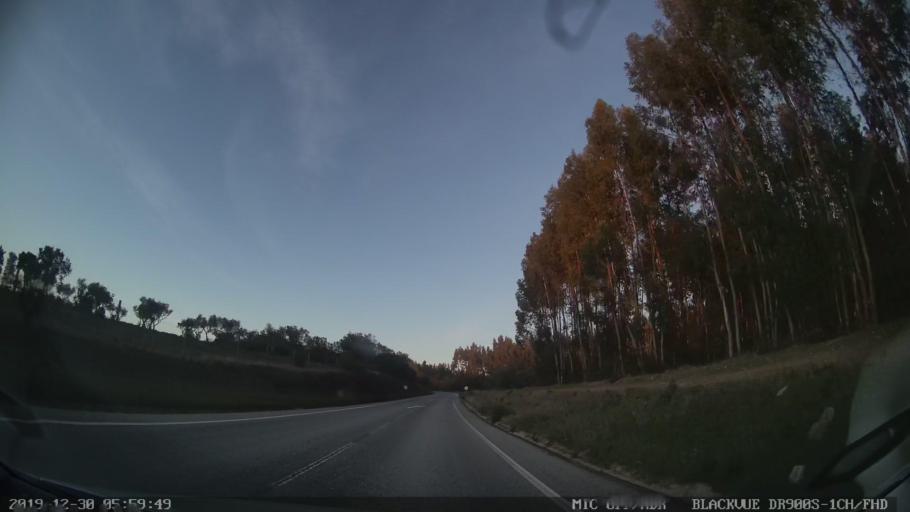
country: PT
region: Castelo Branco
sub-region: Idanha-A-Nova
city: Idanha-a-Nova
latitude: 40.0470
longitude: -7.2437
